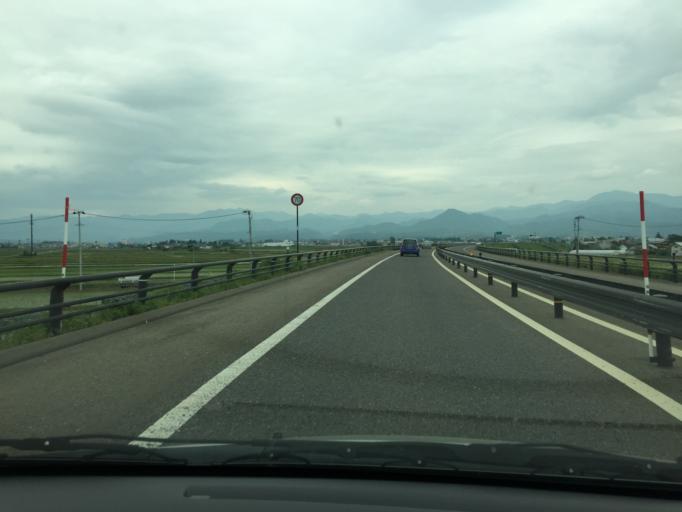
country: JP
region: Fukushima
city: Kitakata
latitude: 37.6294
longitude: 139.8844
